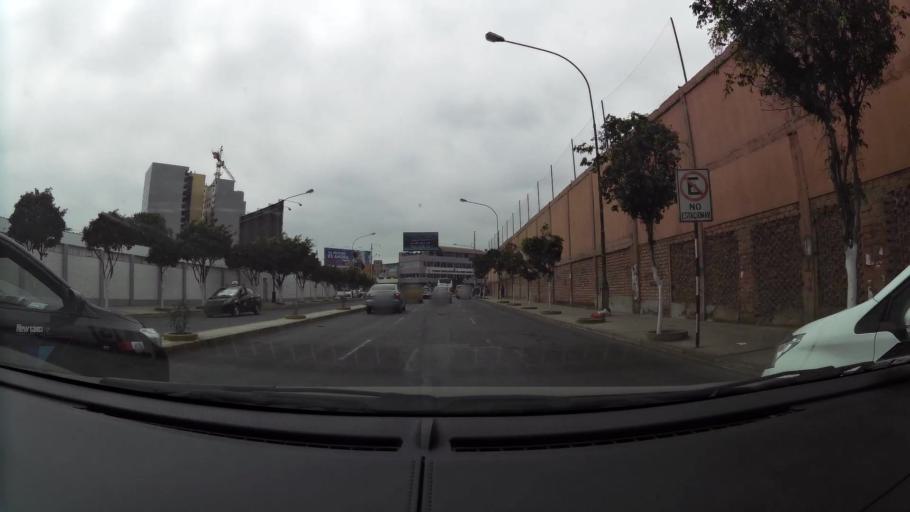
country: PE
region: La Libertad
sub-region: Provincia de Trujillo
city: Trujillo
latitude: -8.1118
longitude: -79.0328
